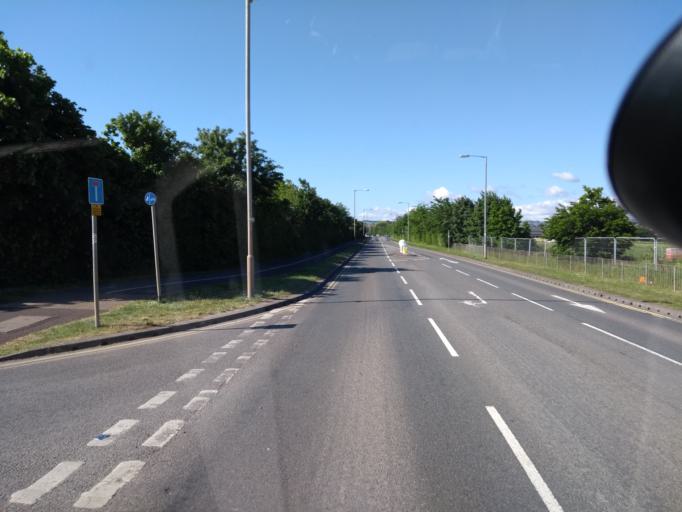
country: GB
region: England
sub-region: Somerset
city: Bridgwater
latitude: 51.1368
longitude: -3.0131
